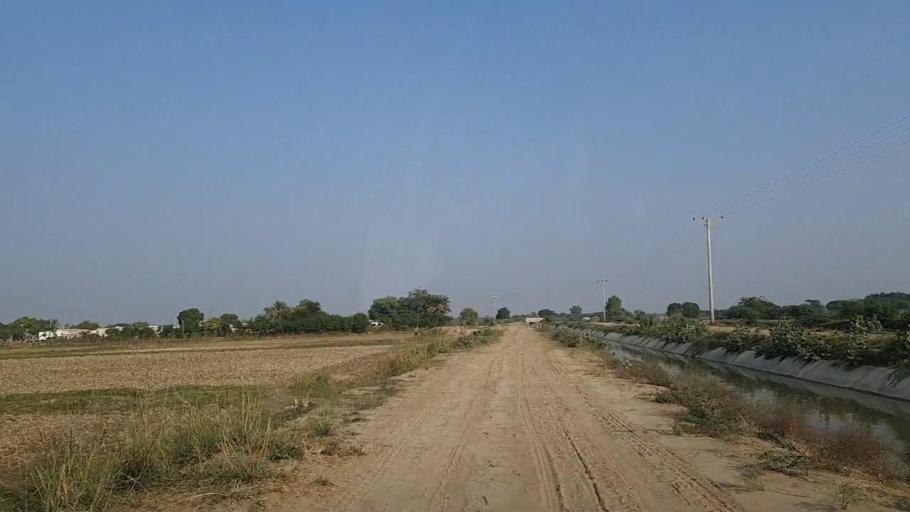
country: PK
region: Sindh
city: Mirpur Sakro
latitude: 24.6155
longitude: 67.7299
